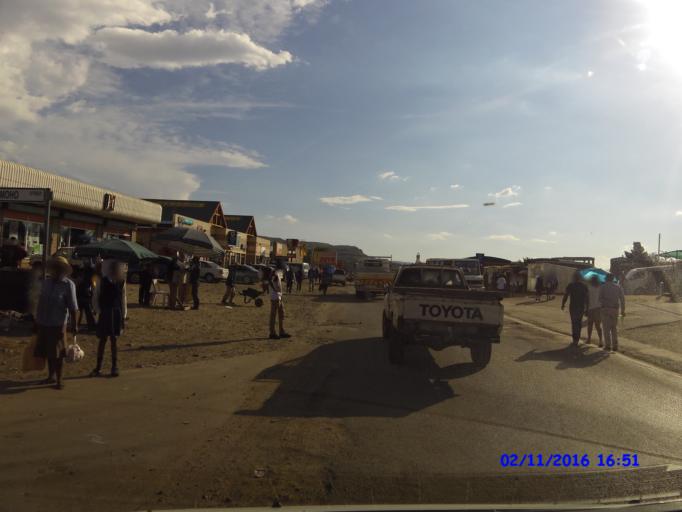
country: LS
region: Butha-Buthe
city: Butha-Buthe
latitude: -28.7686
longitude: 28.2494
